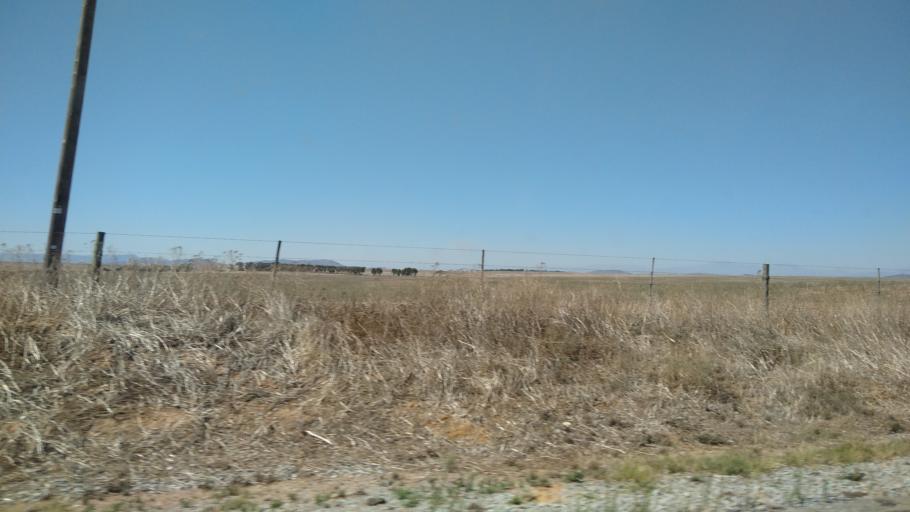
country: ZA
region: Western Cape
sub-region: West Coast District Municipality
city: Moorreesburg
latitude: -33.1773
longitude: 18.4890
